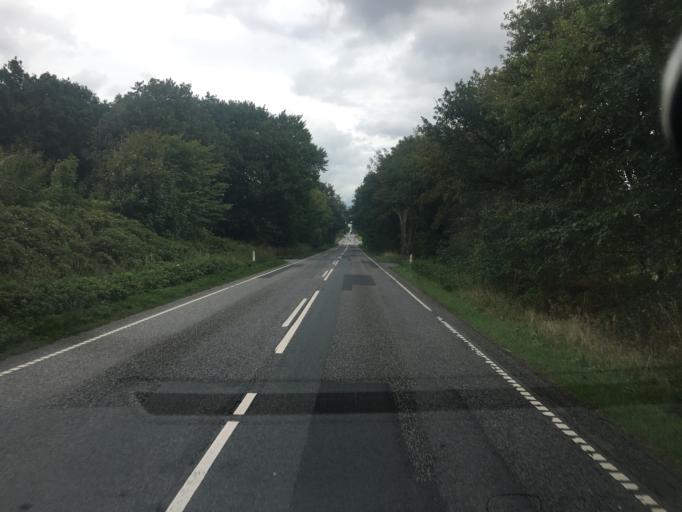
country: DK
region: South Denmark
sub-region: Tonder Kommune
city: Toftlund
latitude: 55.1243
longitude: 9.1146
